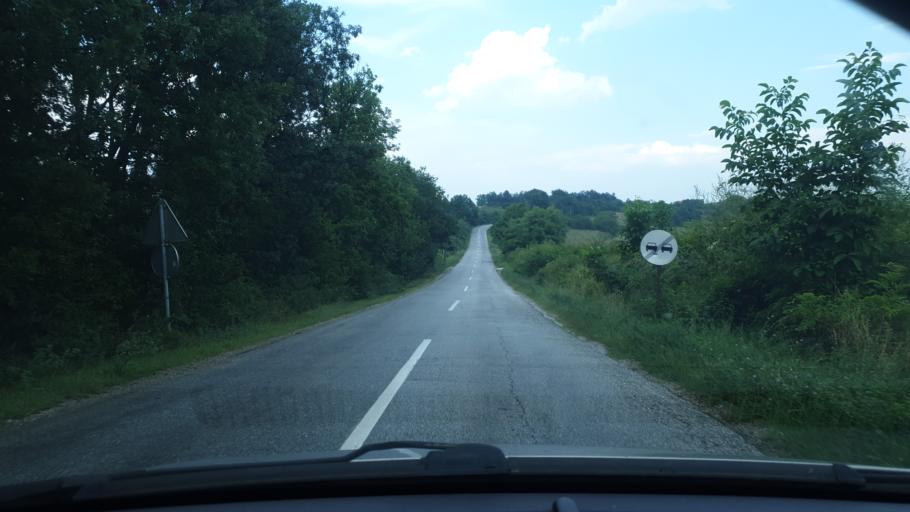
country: RS
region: Central Serbia
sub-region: Sumadijski Okrug
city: Kragujevac
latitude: 44.0453
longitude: 20.7890
